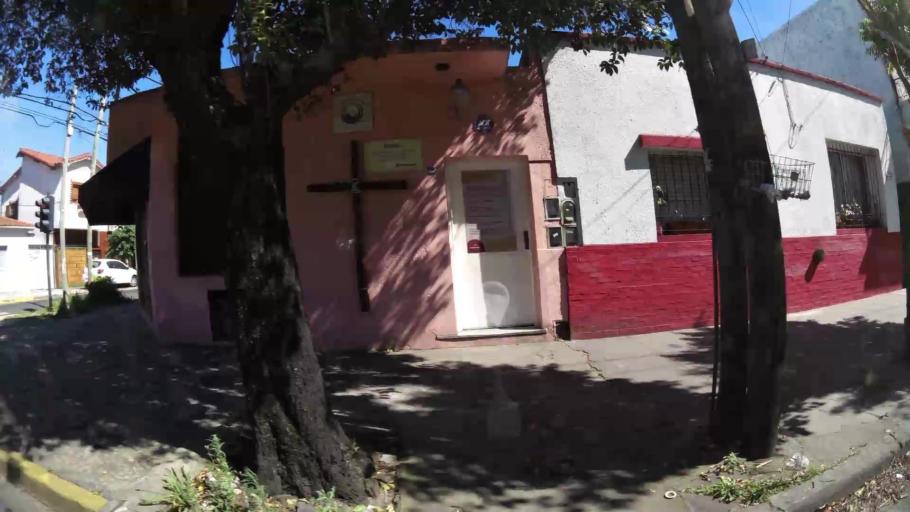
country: AR
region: Buenos Aires
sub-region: Partido de Vicente Lopez
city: Olivos
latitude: -34.5302
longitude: -58.5173
